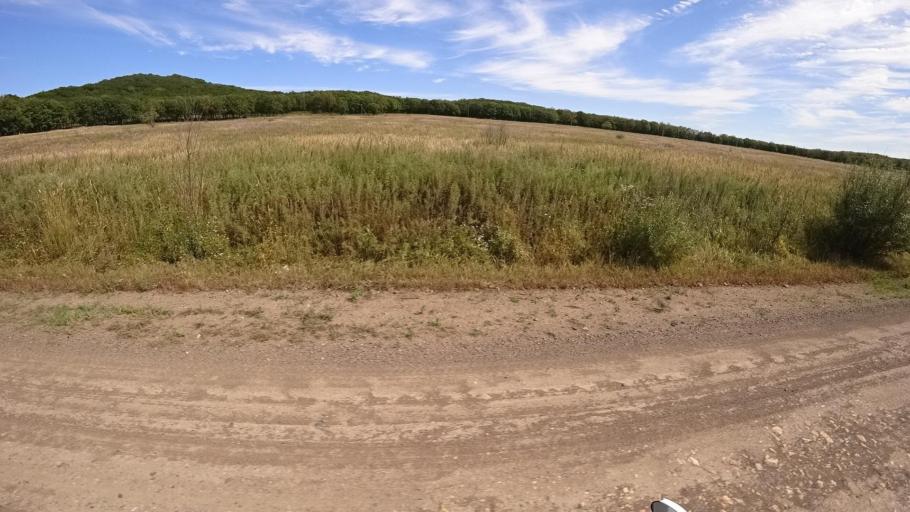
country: RU
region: Primorskiy
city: Yakovlevka
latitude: 44.7266
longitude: 133.6109
